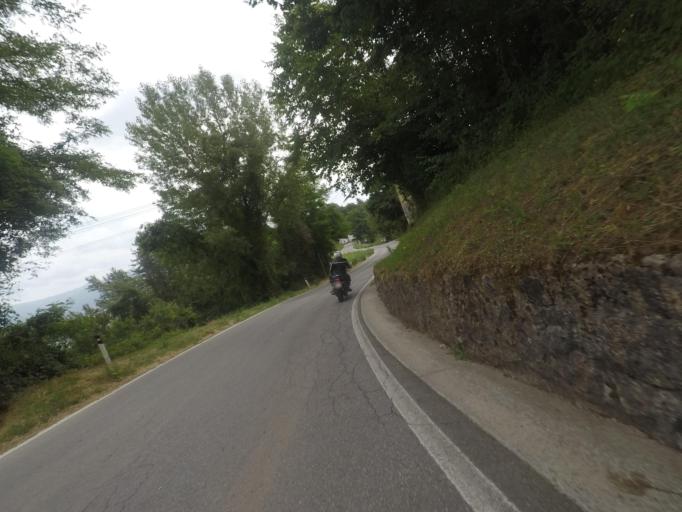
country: IT
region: Tuscany
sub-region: Provincia di Lucca
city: Castelnuovo di Garfagnana
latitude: 44.1121
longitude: 10.3783
